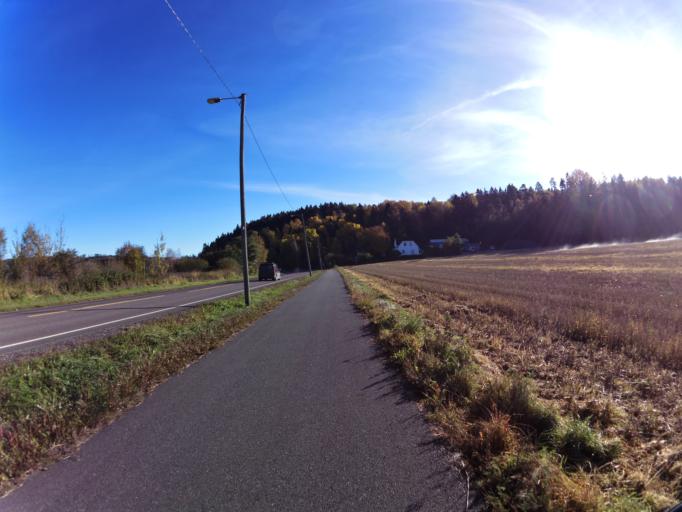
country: NO
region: Ostfold
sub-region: Fredrikstad
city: Fredrikstad
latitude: 59.2986
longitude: 10.9860
